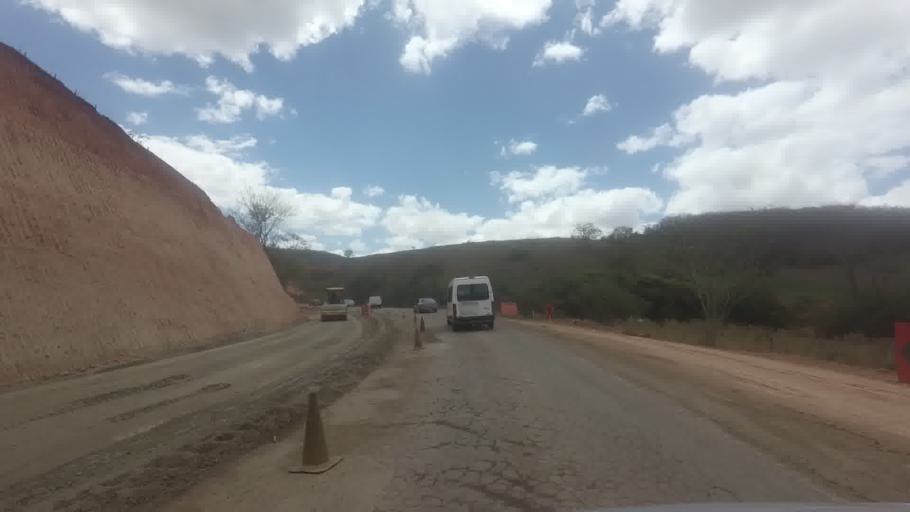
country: BR
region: Rio de Janeiro
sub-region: Santo Antonio De Padua
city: Santo Antonio de Padua
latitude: -21.5136
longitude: -42.0917
